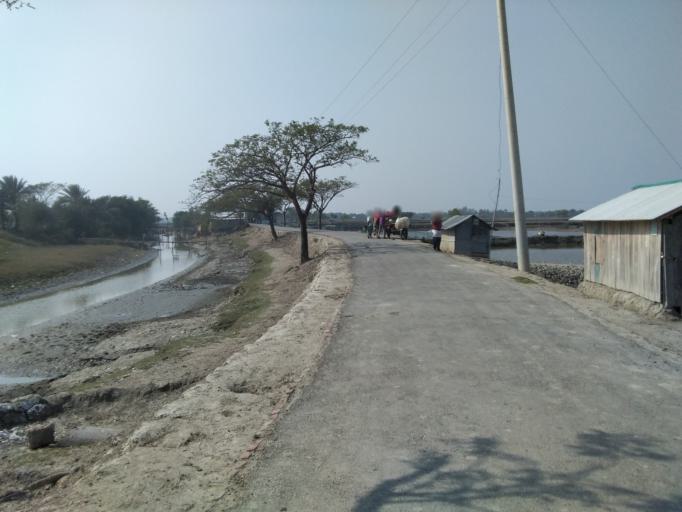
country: IN
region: West Bengal
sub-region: North 24 Parganas
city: Taki
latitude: 22.6345
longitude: 89.0108
